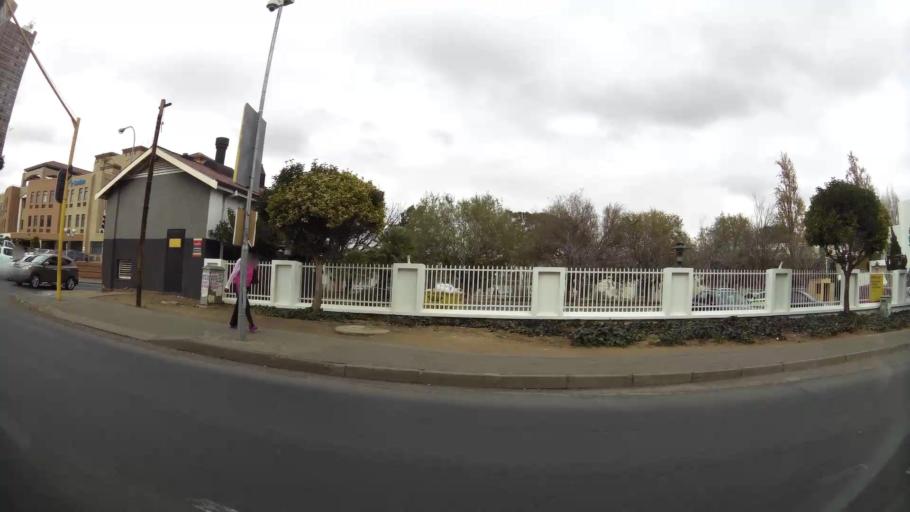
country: ZA
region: Orange Free State
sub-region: Mangaung Metropolitan Municipality
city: Bloemfontein
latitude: -29.1114
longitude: 26.2083
